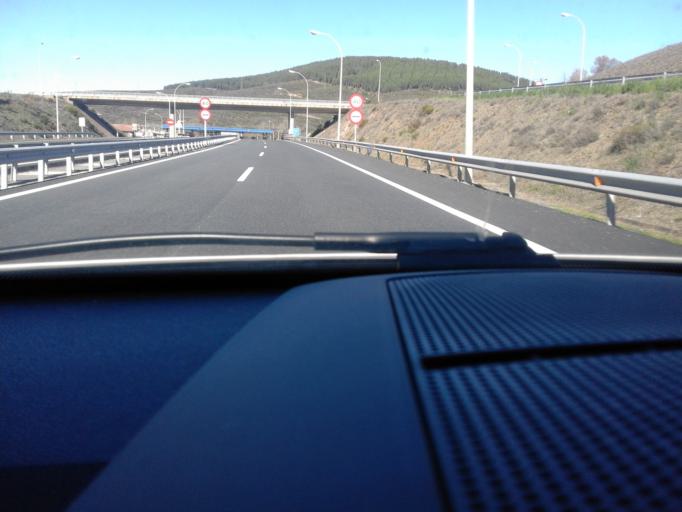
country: ES
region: Castille and Leon
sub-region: Provincia de Leon
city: Carrocera
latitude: 42.7808
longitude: -5.7850
